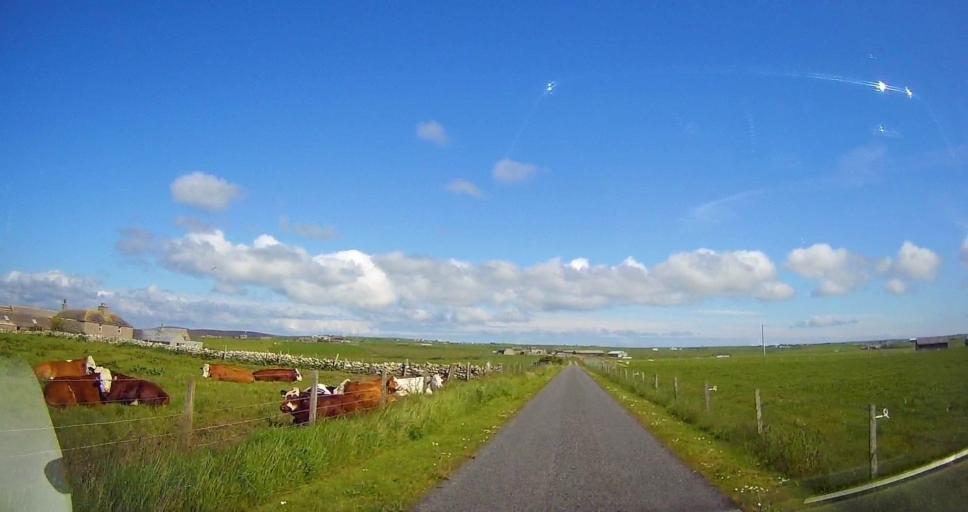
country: GB
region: Scotland
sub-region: Orkney Islands
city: Kirkwall
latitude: 58.8984
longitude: -2.9291
